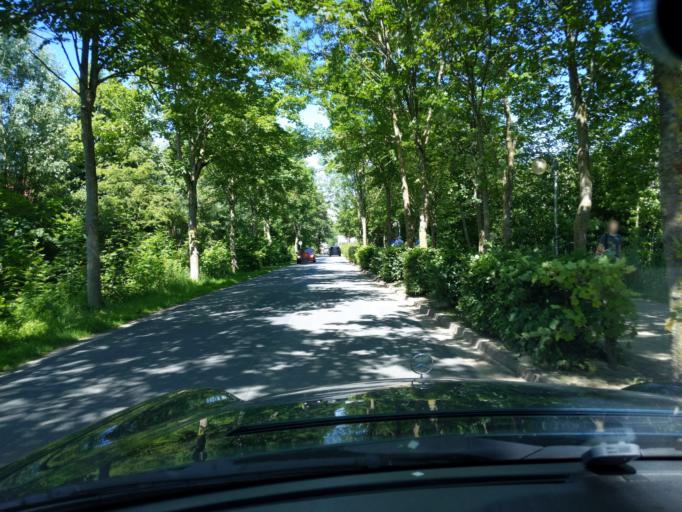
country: DE
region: Lower Saxony
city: Butjadingen
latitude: 53.5742
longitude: 8.2540
